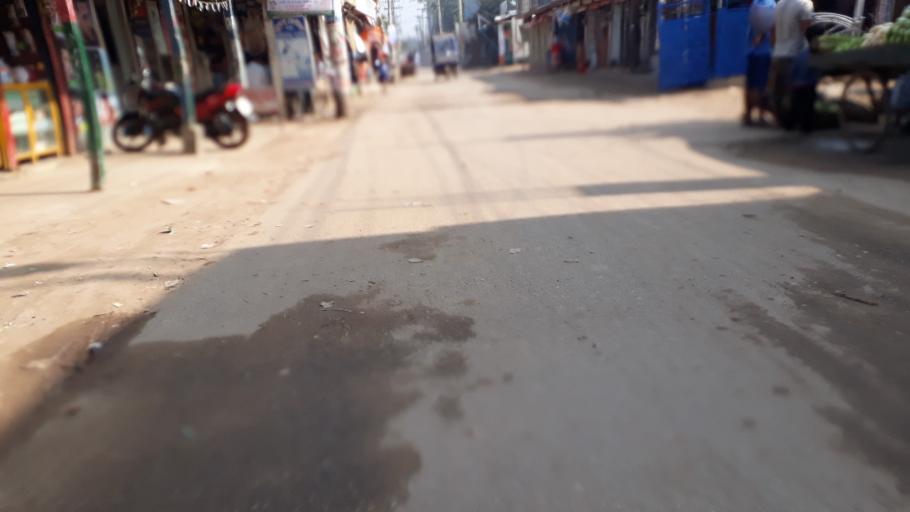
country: BD
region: Dhaka
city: Tungi
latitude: 23.8501
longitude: 90.2833
